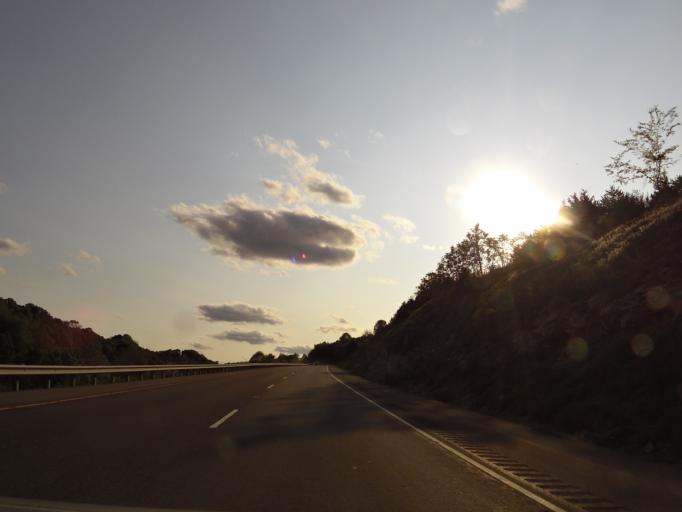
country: US
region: Virginia
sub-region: Tazewell County
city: Claypool Hill
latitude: 36.9999
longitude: -81.8193
